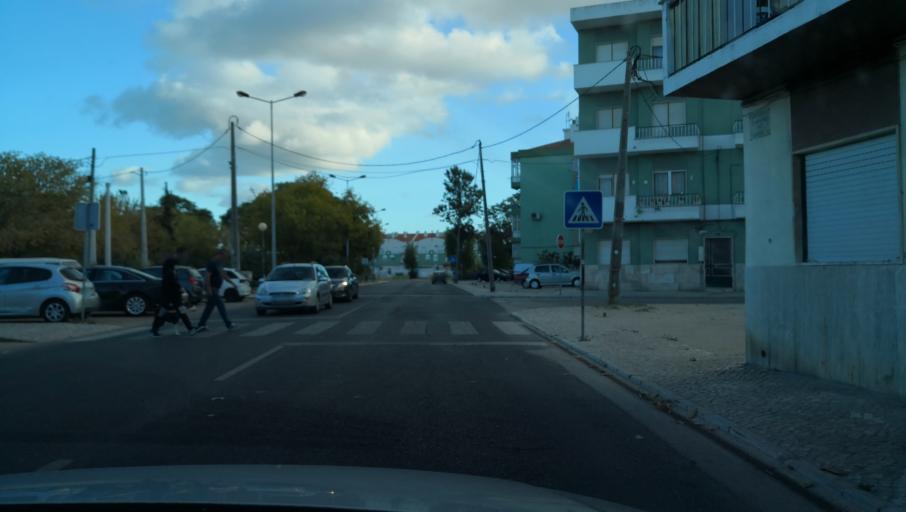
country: PT
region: Setubal
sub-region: Moita
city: Alhos Vedros
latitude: 38.6630
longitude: -9.0436
